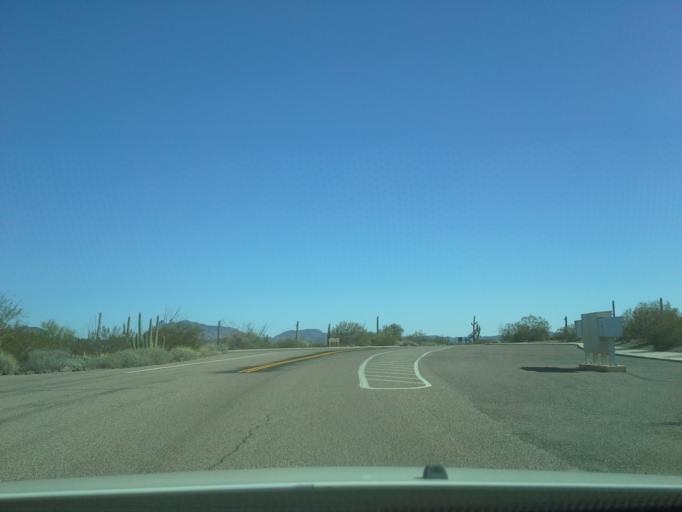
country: MX
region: Sonora
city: Sonoyta
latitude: 31.9542
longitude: -112.8017
